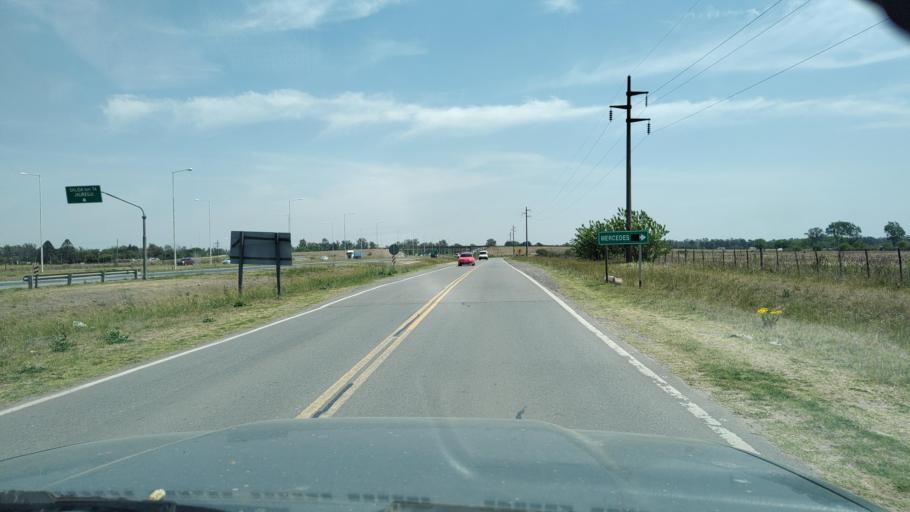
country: AR
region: Buenos Aires
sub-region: Partido de Lujan
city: Lujan
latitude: -34.6057
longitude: -59.1651
